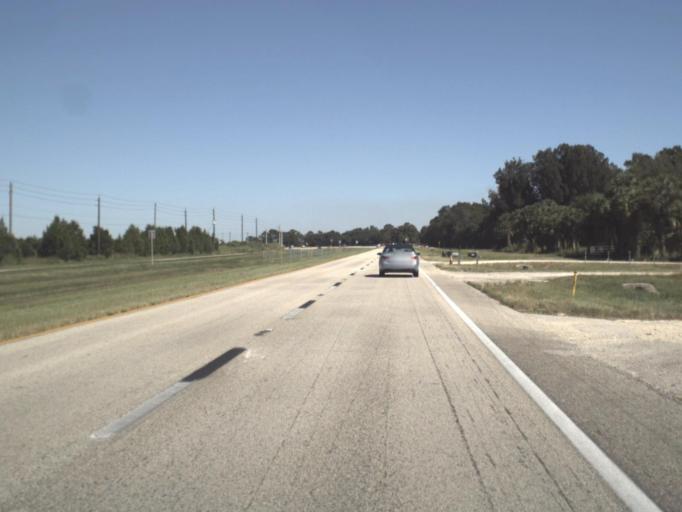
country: US
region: Florida
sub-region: Hendry County
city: LaBelle
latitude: 26.7099
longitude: -81.5151
